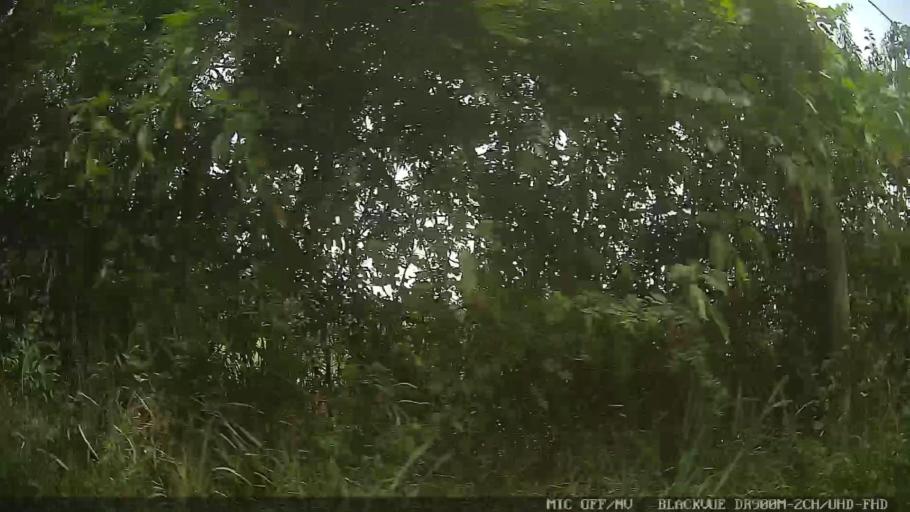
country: BR
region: Sao Paulo
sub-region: Atibaia
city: Atibaia
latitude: -23.0868
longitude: -46.5503
